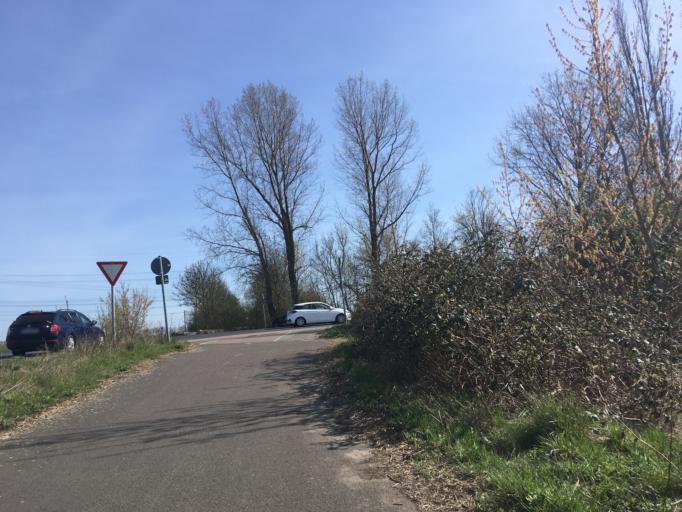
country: DE
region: Berlin
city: Wartenberg
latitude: 52.5967
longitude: 13.5046
